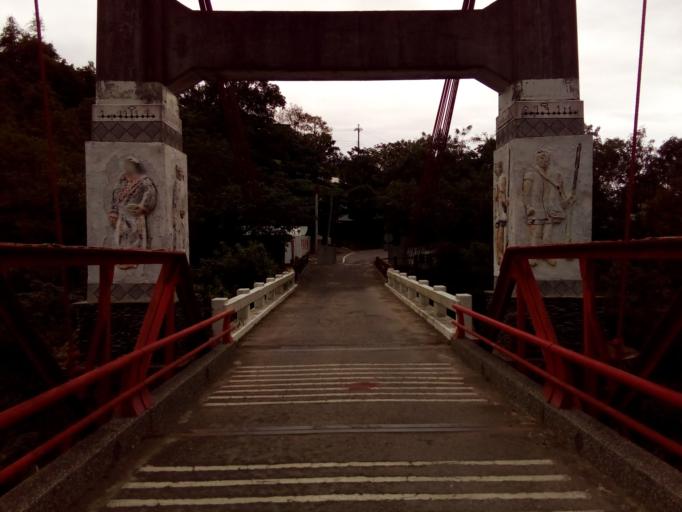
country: TW
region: Taiwan
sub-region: Taitung
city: Taitung
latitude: 22.8982
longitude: 121.0850
